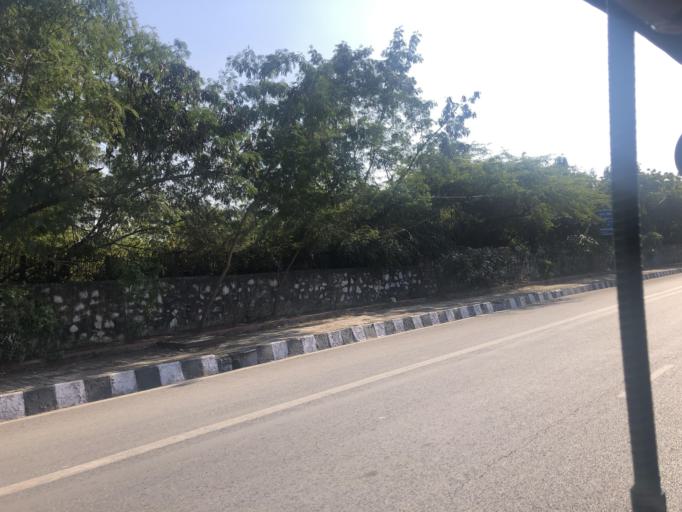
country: IN
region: NCT
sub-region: Central Delhi
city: Karol Bagh
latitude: 28.5453
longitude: 77.1604
